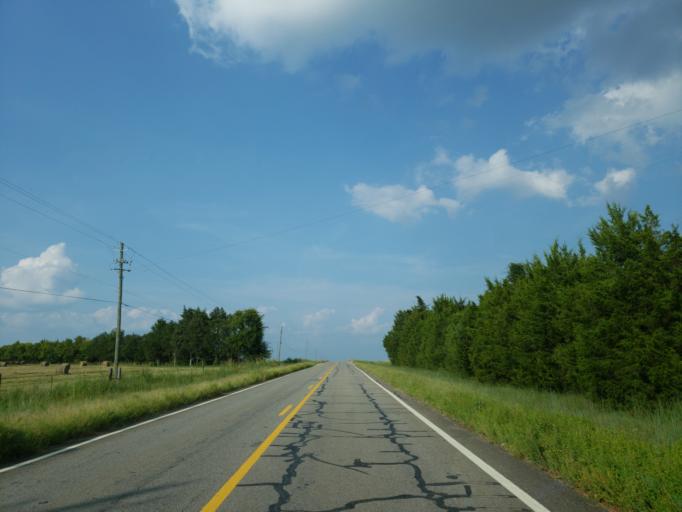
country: US
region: Alabama
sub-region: Greene County
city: Eutaw
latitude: 32.8036
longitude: -87.9568
